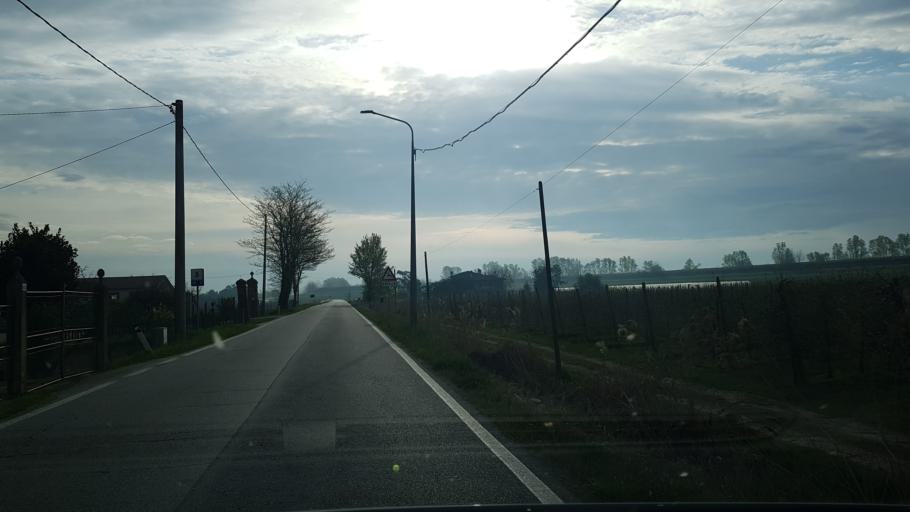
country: IT
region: Veneto
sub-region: Provincia di Padova
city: Piacenza d'Adige
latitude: 45.1251
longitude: 11.5653
